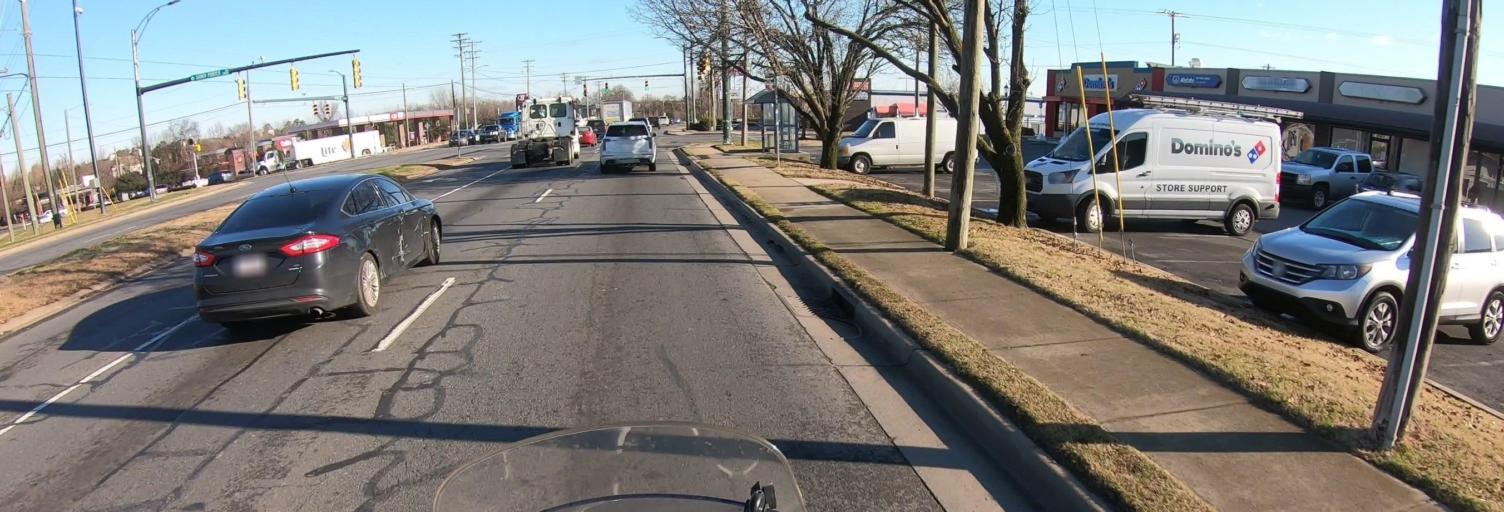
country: US
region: North Carolina
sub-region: Mecklenburg County
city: Pineville
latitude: 35.1340
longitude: -80.9395
